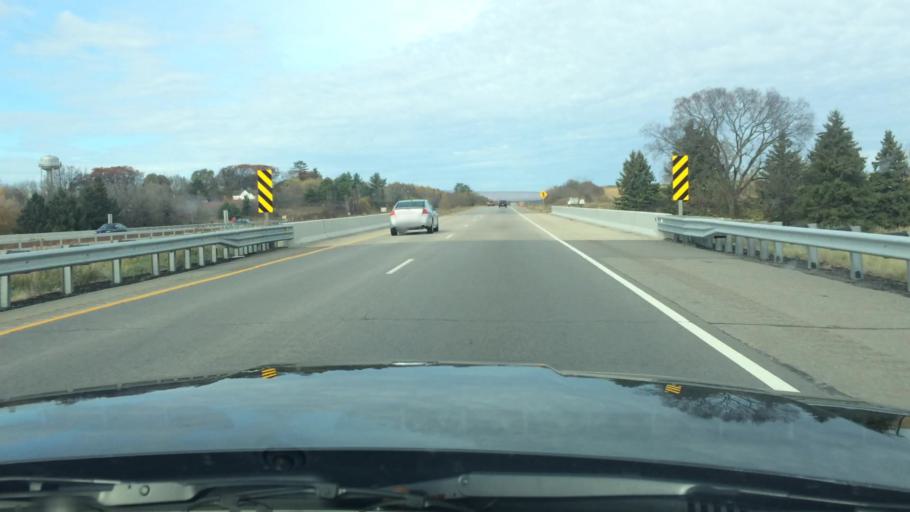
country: US
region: Wisconsin
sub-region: Marathon County
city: Mosinee
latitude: 44.7856
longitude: -89.6802
